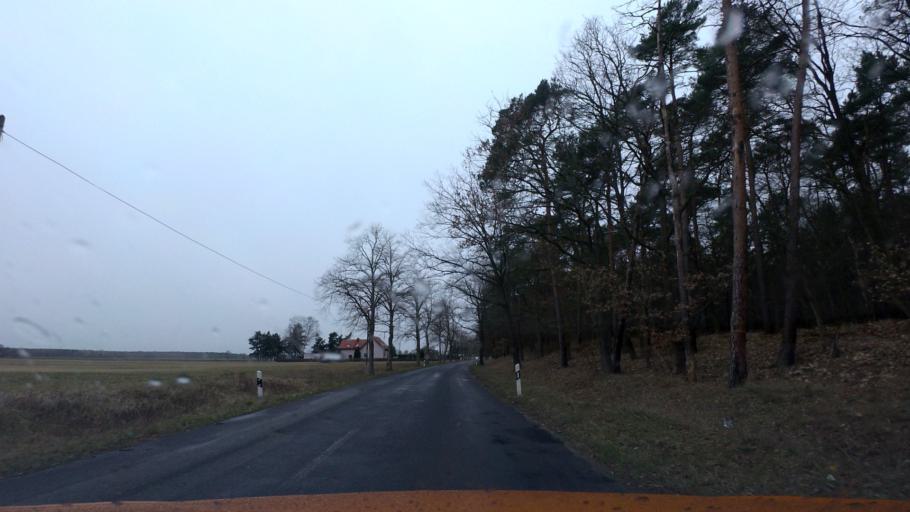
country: DE
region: Brandenburg
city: Brieselang
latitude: 52.6409
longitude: 13.0356
